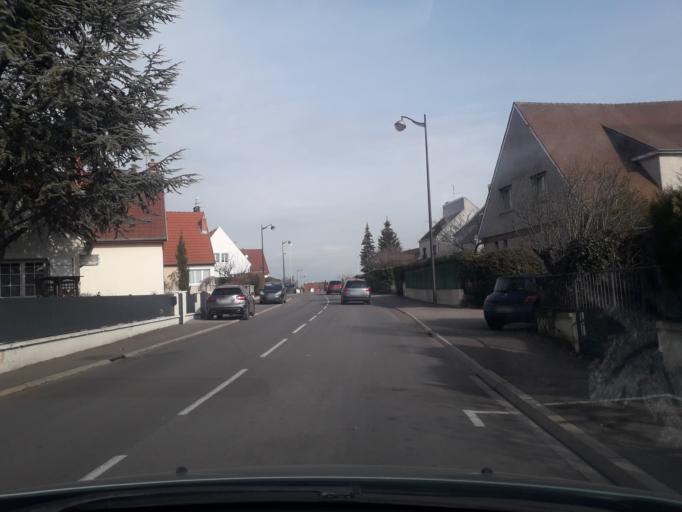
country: FR
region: Bourgogne
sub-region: Departement de la Cote-d'Or
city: Fontaine-les-Dijon
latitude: 47.3443
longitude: 5.0237
